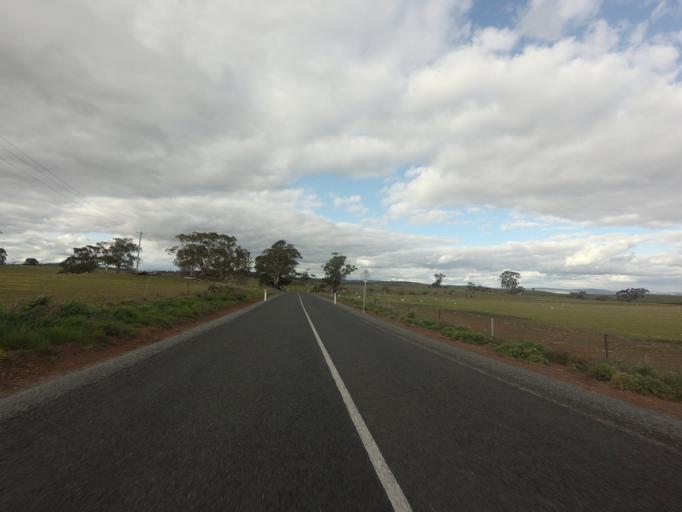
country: AU
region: Tasmania
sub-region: Northern Midlands
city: Evandale
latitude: -41.9085
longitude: 147.3858
